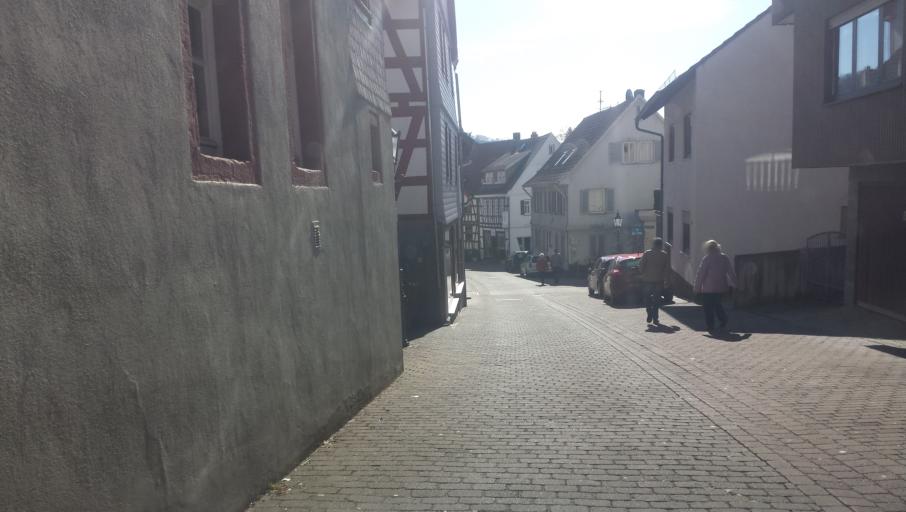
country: DE
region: Hesse
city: Reichelsheim
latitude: 49.7148
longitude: 8.8392
